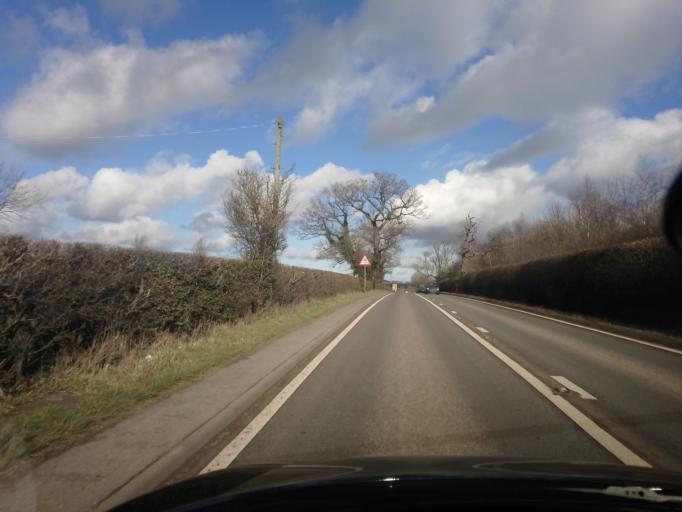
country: GB
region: England
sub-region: Shropshire
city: Astley
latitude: 52.7658
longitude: -2.7152
